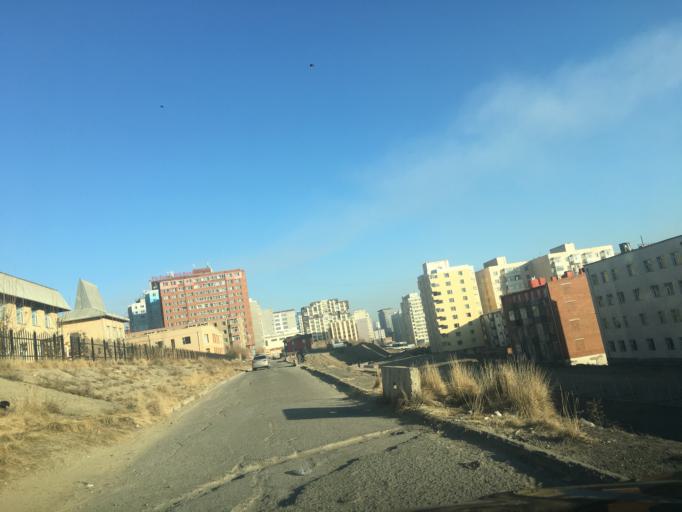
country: MN
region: Ulaanbaatar
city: Ulaanbaatar
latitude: 47.9173
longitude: 106.8782
